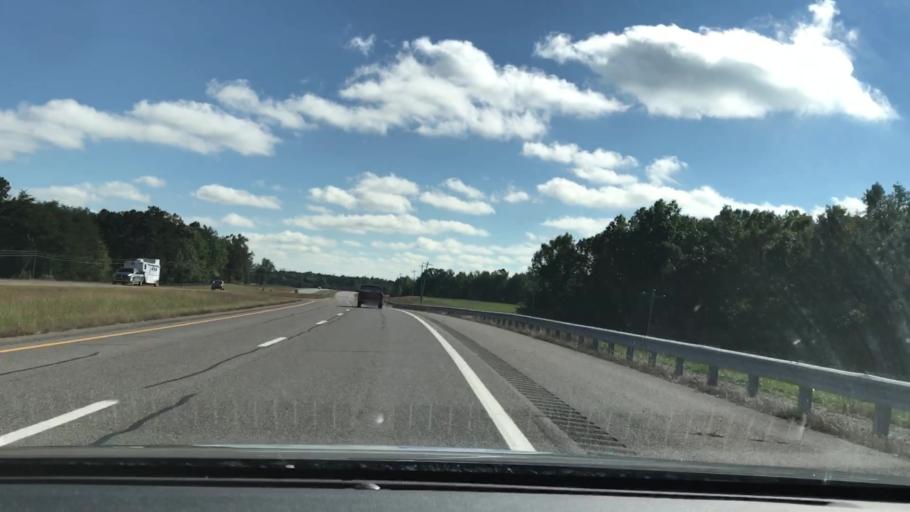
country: US
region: Tennessee
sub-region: Fentress County
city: Jamestown
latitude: 36.3490
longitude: -84.9525
